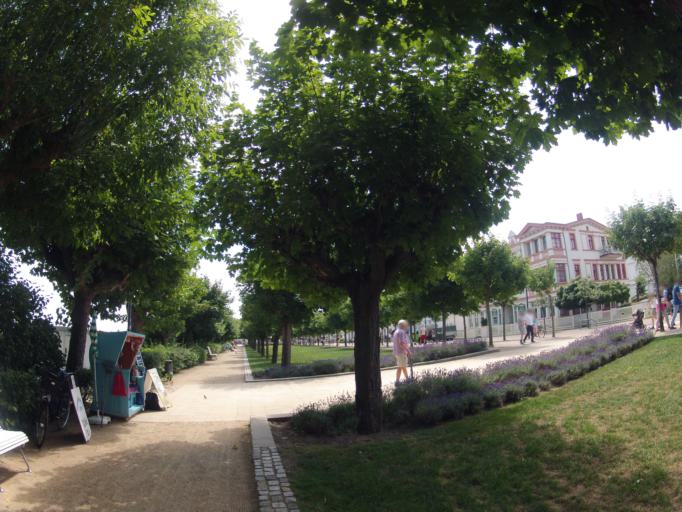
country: DE
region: Mecklenburg-Vorpommern
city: Seebad Heringsdorf
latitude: 53.9395
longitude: 14.1956
